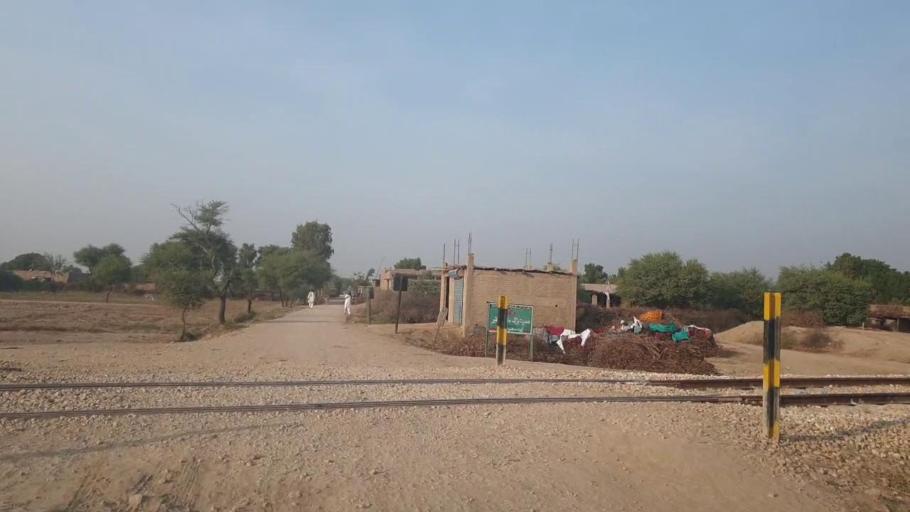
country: PK
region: Sindh
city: Tando Jam
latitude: 25.4399
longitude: 68.5620
